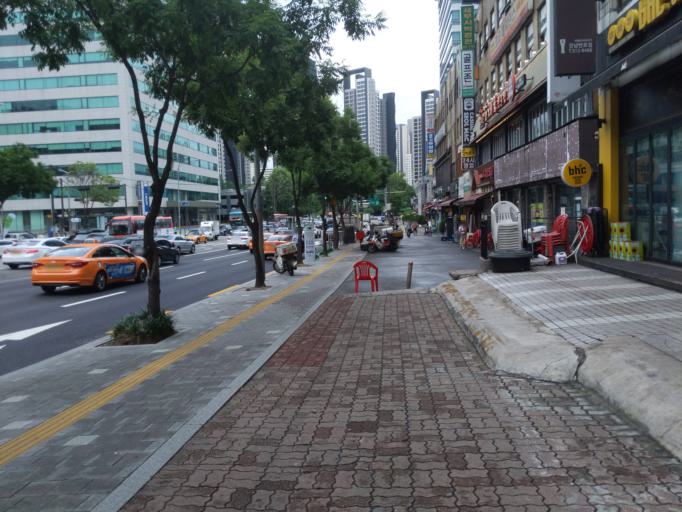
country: KR
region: Seoul
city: Seoul
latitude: 37.5038
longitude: 127.0218
